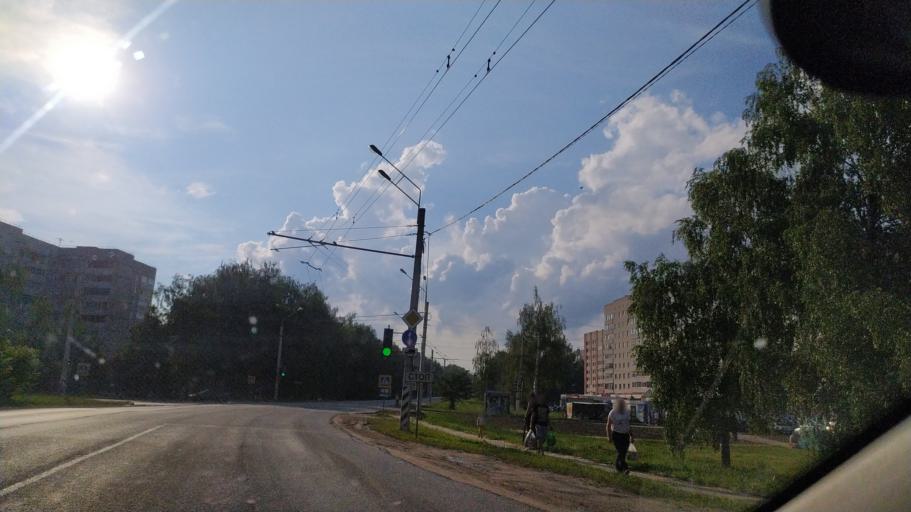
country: RU
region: Chuvashia
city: Novocheboksarsk
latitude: 56.1107
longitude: 47.4462
